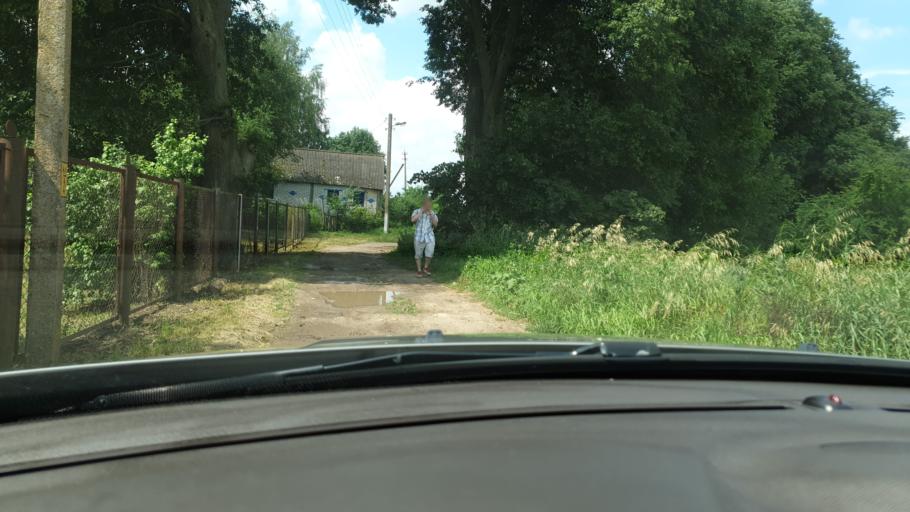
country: BY
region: Grodnenskaya
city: Mir
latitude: 53.3858
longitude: 26.3556
